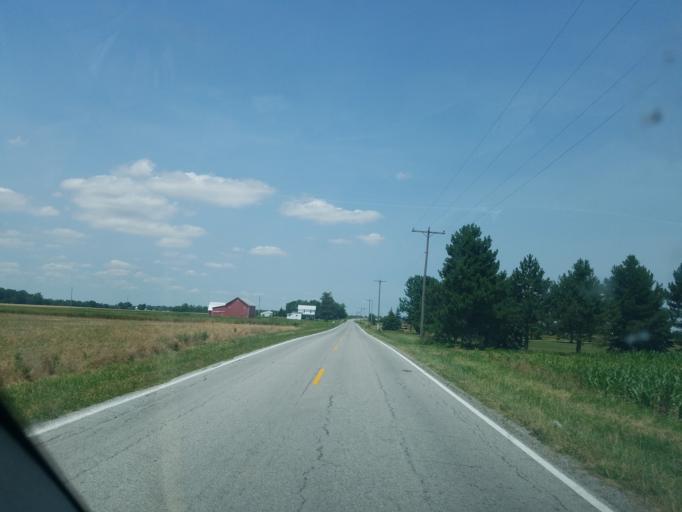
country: US
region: Ohio
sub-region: Wyandot County
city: Carey
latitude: 40.9608
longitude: -83.4860
